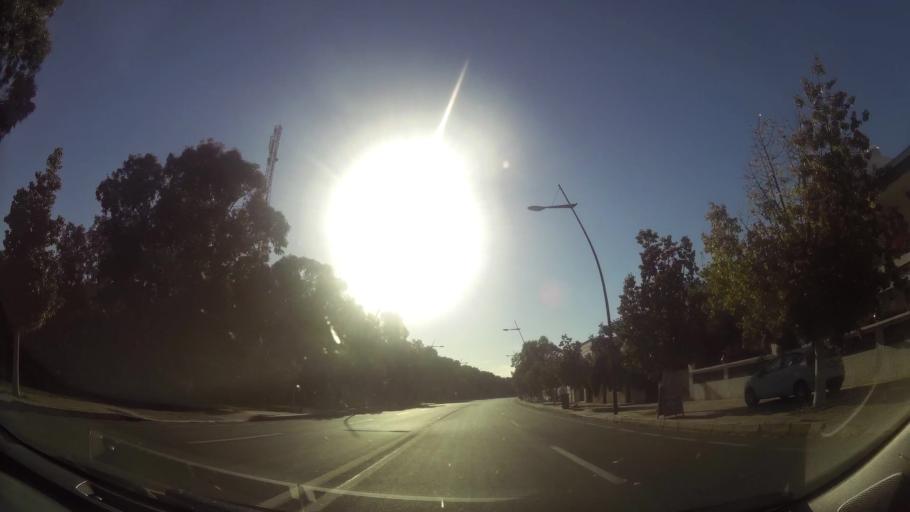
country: MA
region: Oriental
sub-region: Berkane-Taourirt
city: Madagh
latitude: 35.0910
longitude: -2.2530
